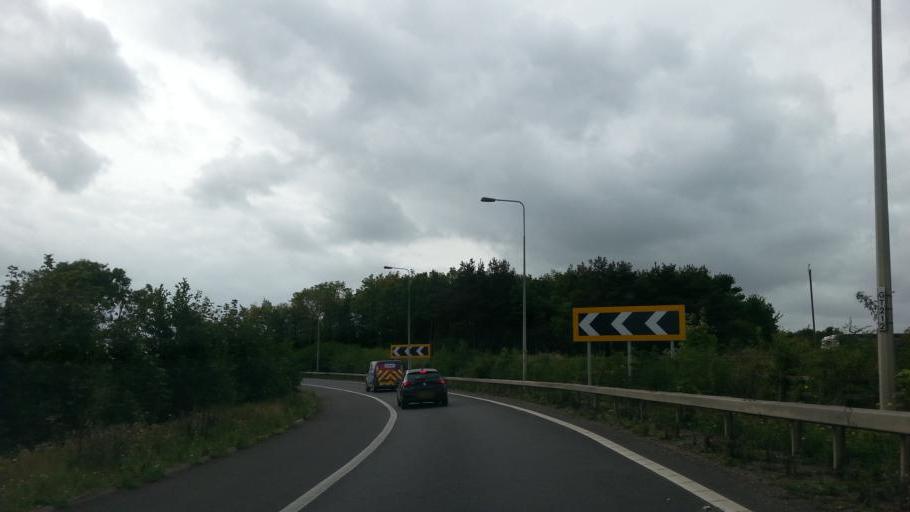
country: GB
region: England
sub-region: Cambridgeshire
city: Girton
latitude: 52.2308
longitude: 0.0735
